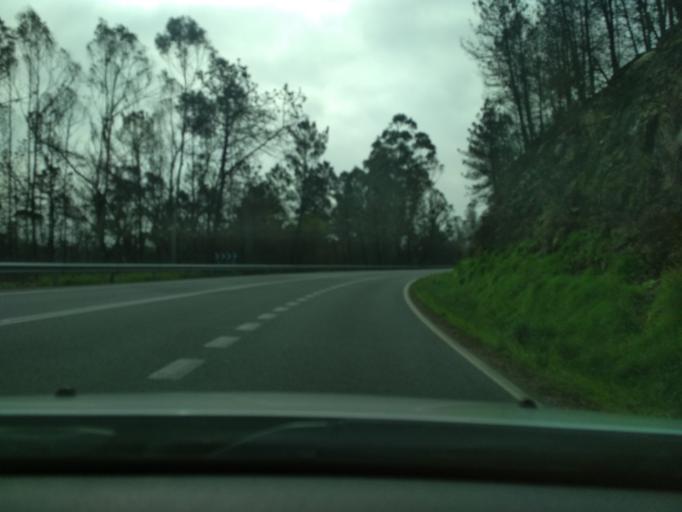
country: ES
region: Galicia
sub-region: Provincia de Pontevedra
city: Catoira
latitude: 42.6529
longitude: -8.6811
